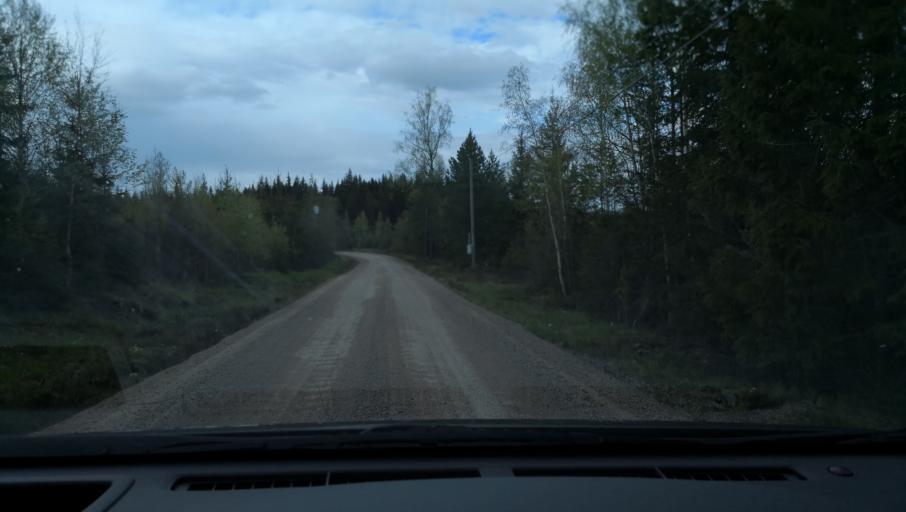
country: SE
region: Vaestmanland
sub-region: Fagersta Kommun
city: Fagersta
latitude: 60.1130
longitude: 15.7990
